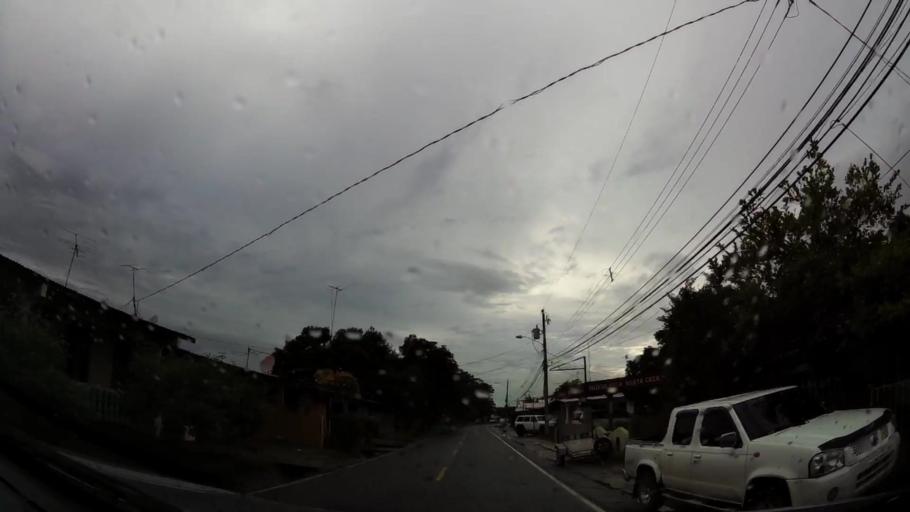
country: PA
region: Veraguas
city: Santiago de Veraguas
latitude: 8.1006
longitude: -80.9732
